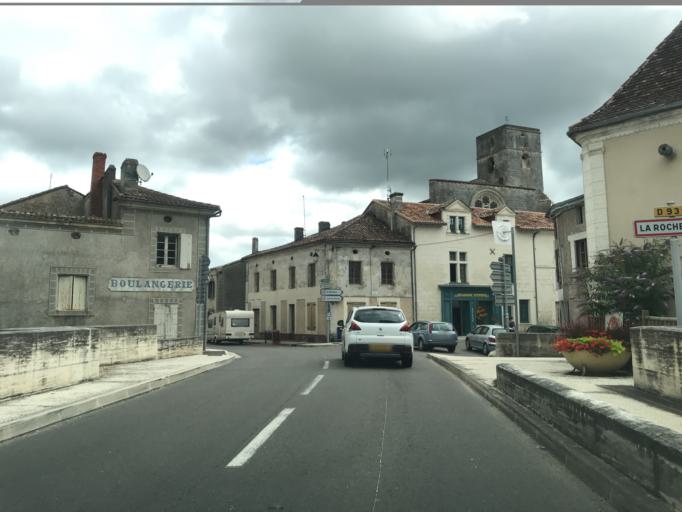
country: FR
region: Aquitaine
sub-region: Departement de la Dordogne
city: Mareuil
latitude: 45.4841
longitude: 0.3784
